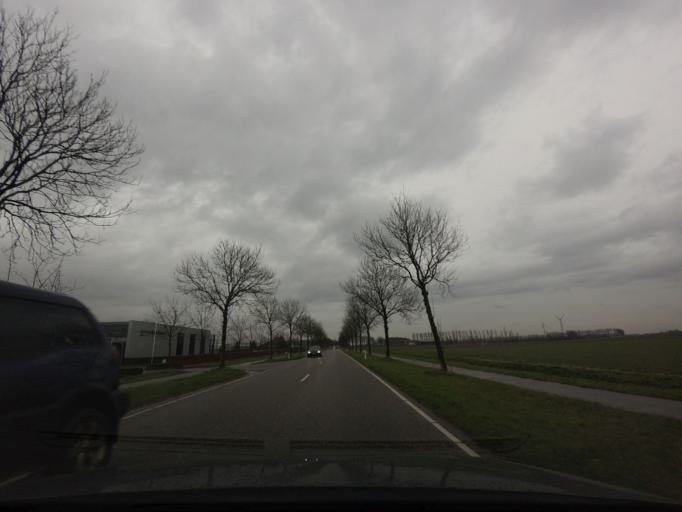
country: NL
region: North Brabant
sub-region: Gemeente Moerdijk
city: Klundert
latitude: 51.6326
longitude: 4.6241
